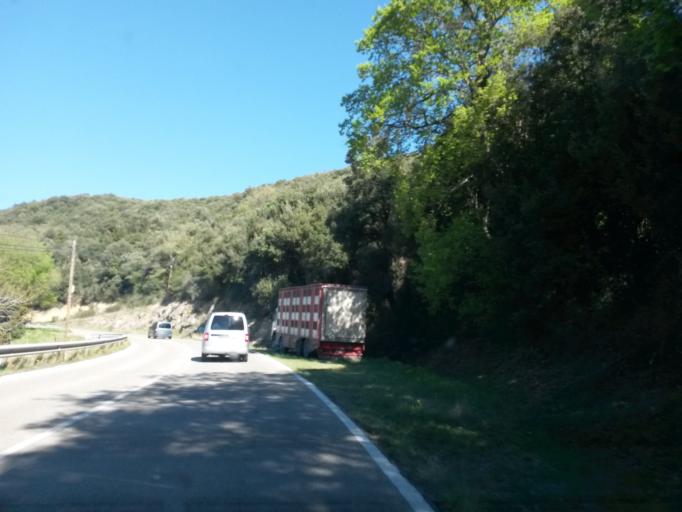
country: ES
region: Catalonia
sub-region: Provincia de Girona
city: Santa Pau
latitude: 42.1473
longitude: 2.5554
